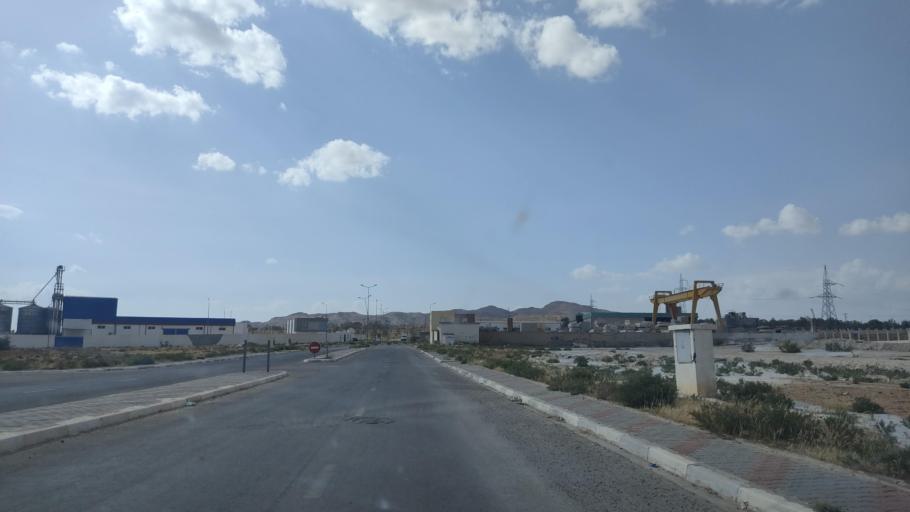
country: TN
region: Sidi Bu Zayd
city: Sidi Bouzid
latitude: 35.1066
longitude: 9.5446
